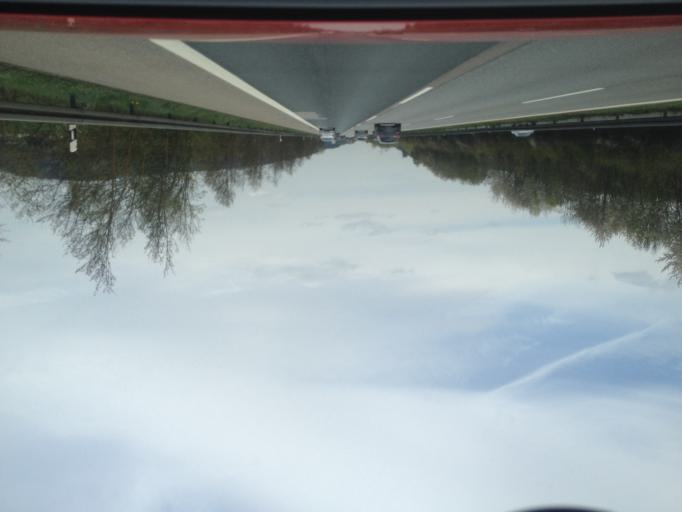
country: DE
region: Bavaria
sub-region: Regierungsbezirk Mittelfranken
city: Thalmassing
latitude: 49.0852
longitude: 11.2887
